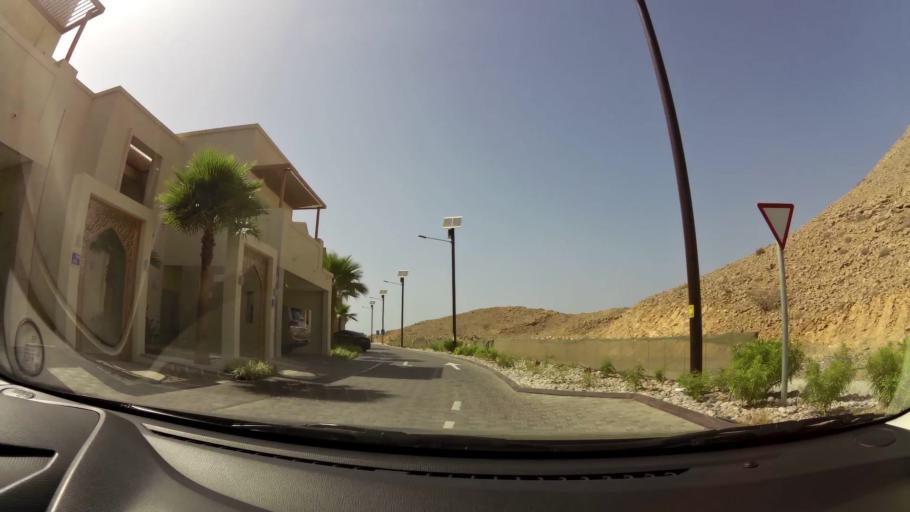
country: OM
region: Muhafazat Masqat
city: Muscat
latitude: 23.6419
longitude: 58.5049
